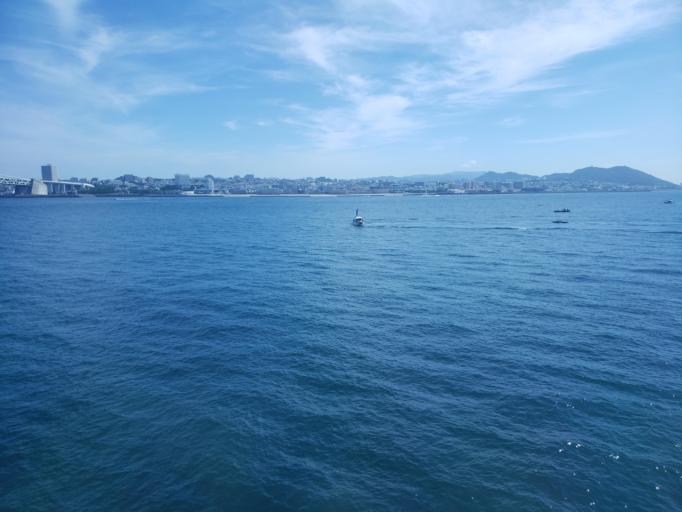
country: JP
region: Hyogo
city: Akashi
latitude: 34.6138
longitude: 135.0314
